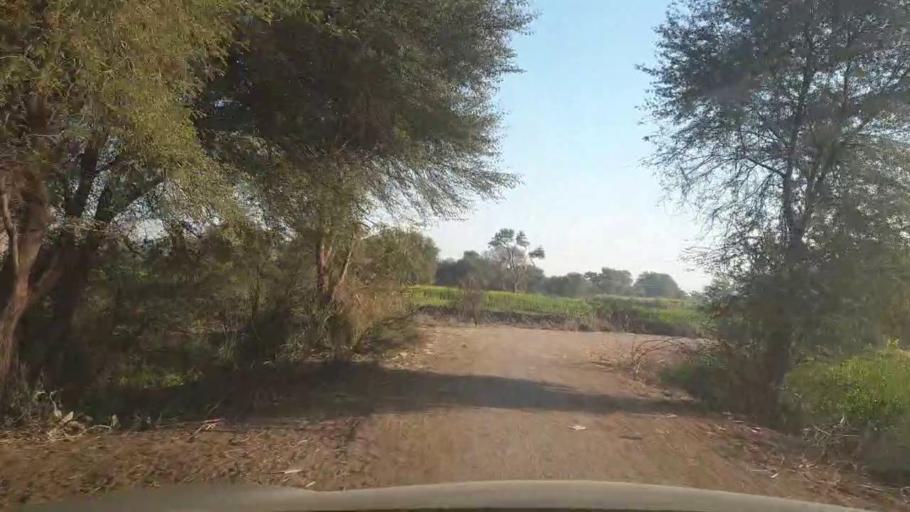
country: PK
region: Sindh
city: Ghotki
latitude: 28.0958
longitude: 69.3630
